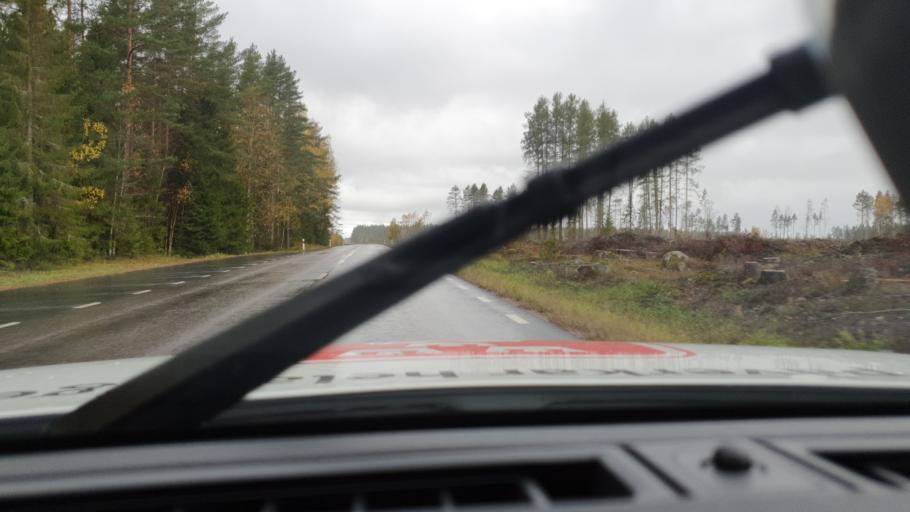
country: SE
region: Uppsala
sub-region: Tierps Kommun
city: Karlholmsbruk
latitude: 60.5448
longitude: 17.5362
